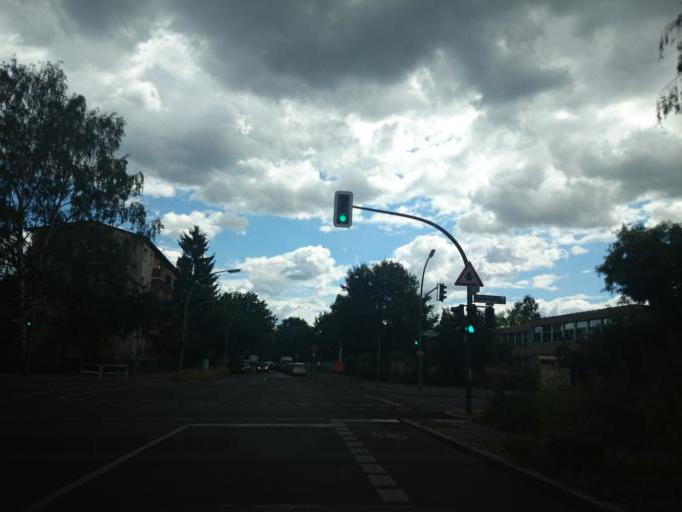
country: DE
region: Berlin
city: Mariendorf
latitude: 52.4340
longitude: 13.3828
